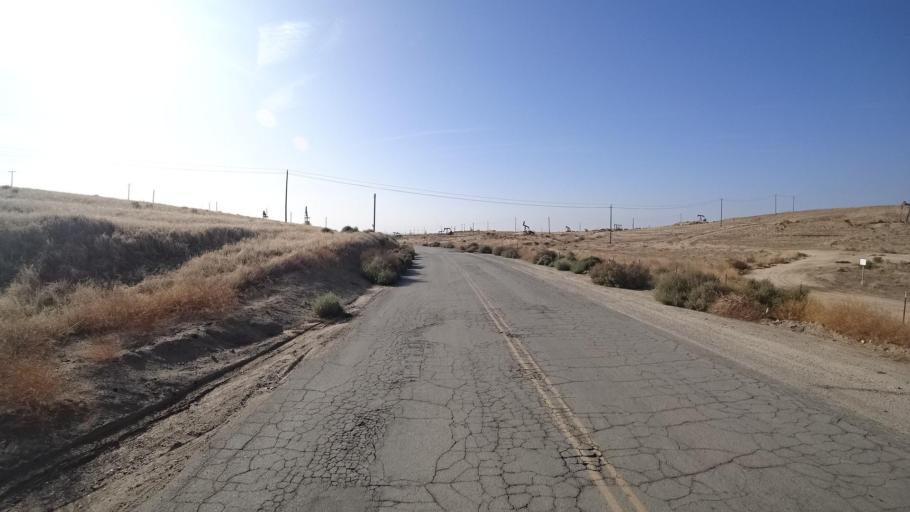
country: US
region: California
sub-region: Kern County
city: Oildale
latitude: 35.4709
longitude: -119.0480
